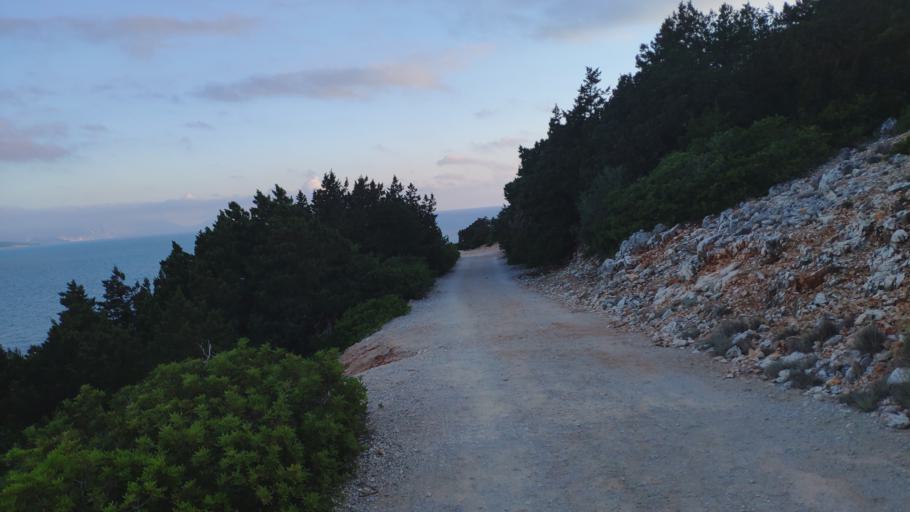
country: GR
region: Ionian Islands
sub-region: Lefkada
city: Nidri
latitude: 38.5631
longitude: 20.5427
